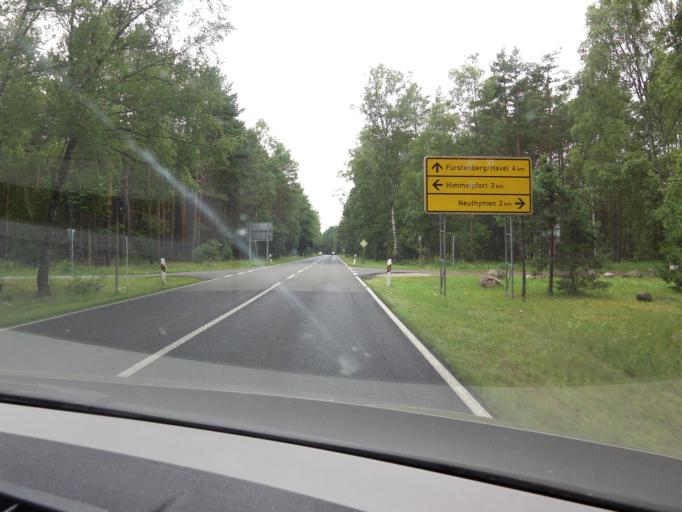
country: DE
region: Brandenburg
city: Furstenberg
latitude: 53.1997
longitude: 13.2033
